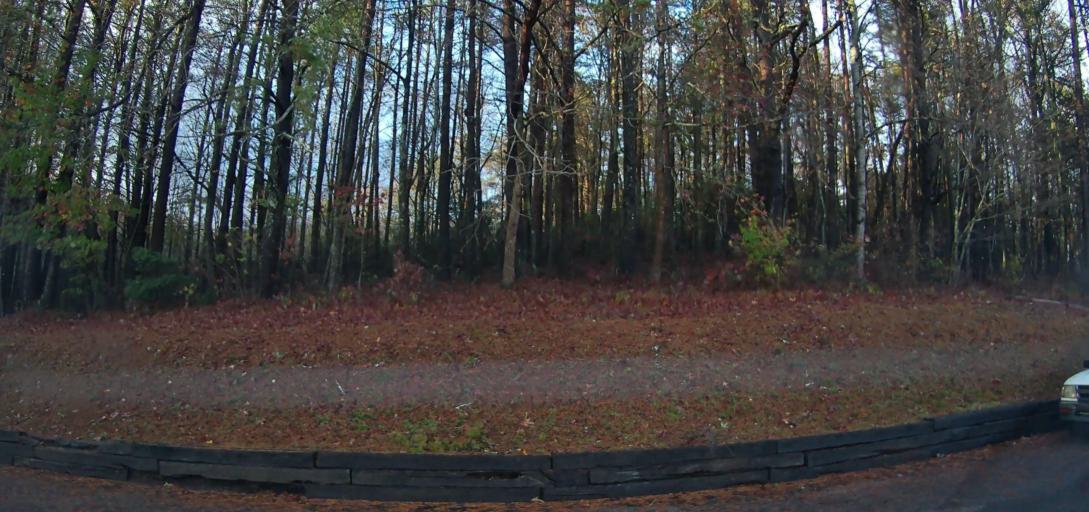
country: US
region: Georgia
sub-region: White County
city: Cleveland
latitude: 34.6538
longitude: -83.7987
